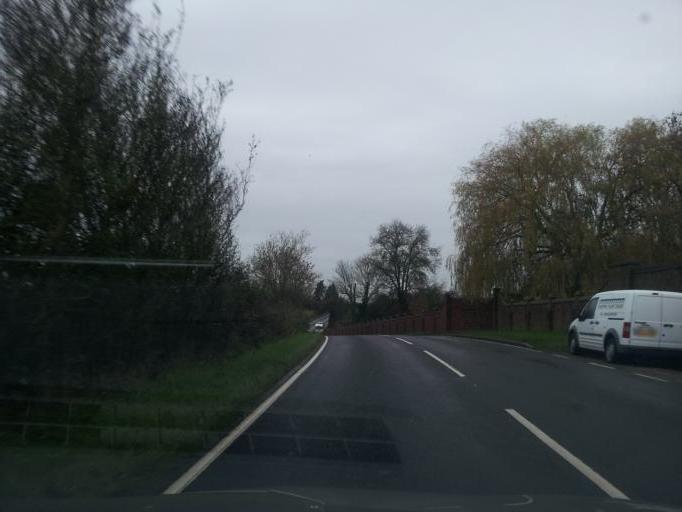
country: GB
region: England
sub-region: Essex
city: Marks Tey
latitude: 51.9153
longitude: 0.7695
